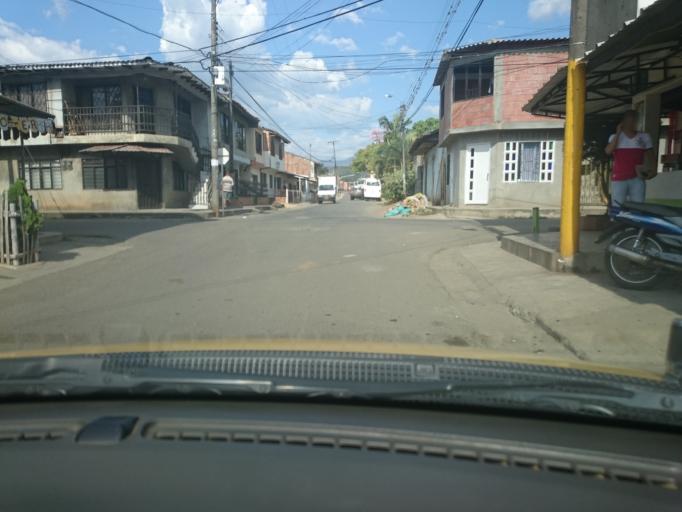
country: CO
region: Cauca
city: Santander de Quilichao
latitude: 3.0163
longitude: -76.4835
